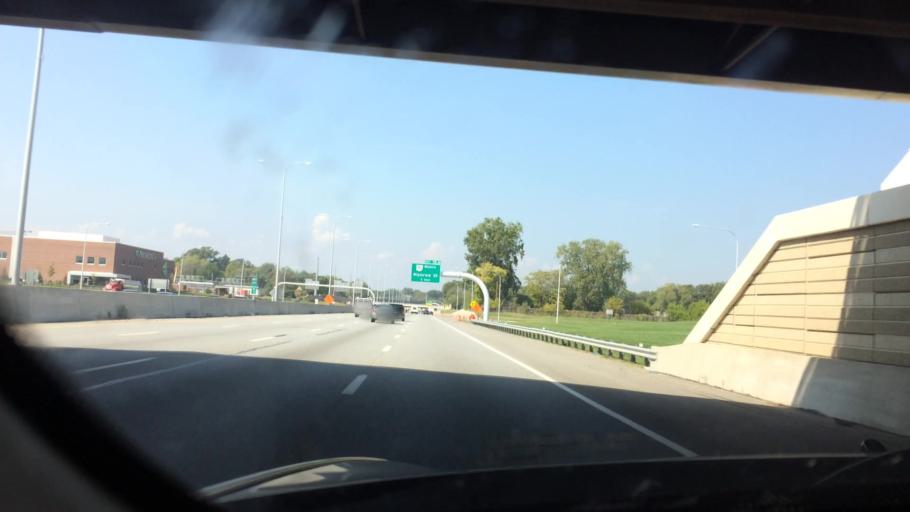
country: US
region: Ohio
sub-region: Lucas County
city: Toledo
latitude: 41.6799
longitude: -83.5910
